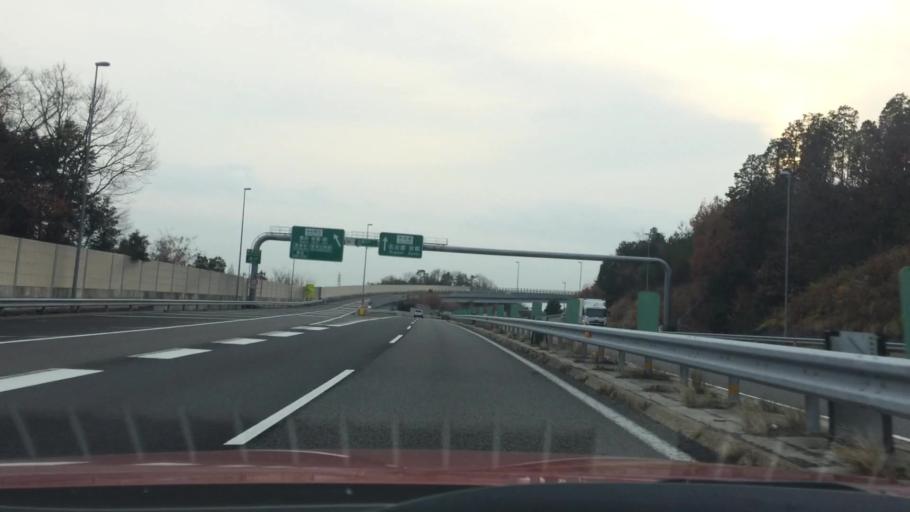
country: JP
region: Gifu
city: Toki
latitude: 35.3655
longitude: 137.1746
